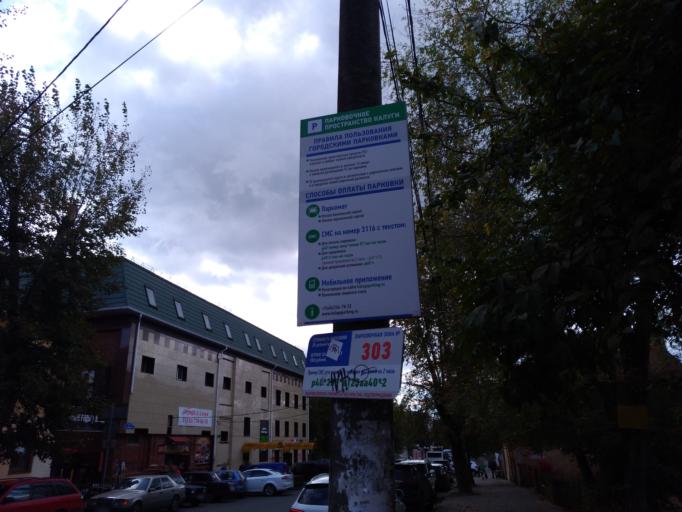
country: RU
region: Kaluga
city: Kaluga
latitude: 54.5167
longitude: 36.2544
